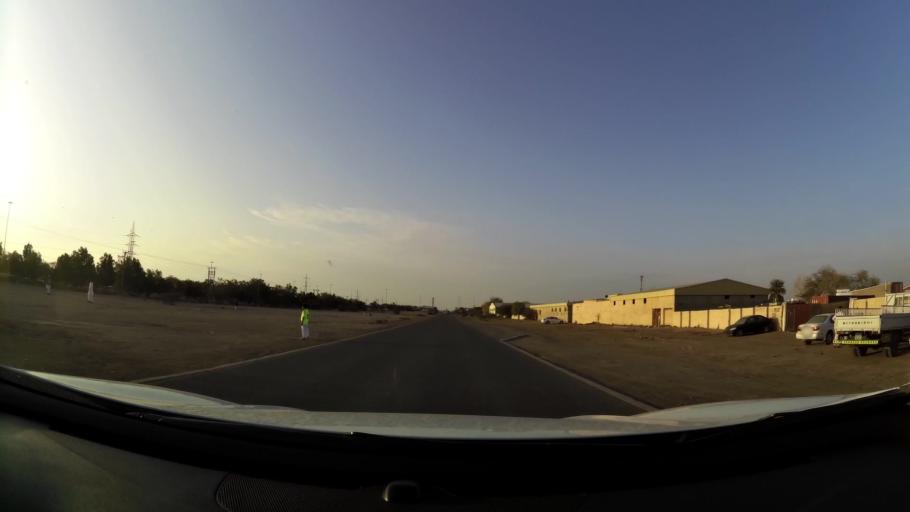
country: AE
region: Abu Dhabi
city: Al Ain
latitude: 24.1454
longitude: 55.8135
